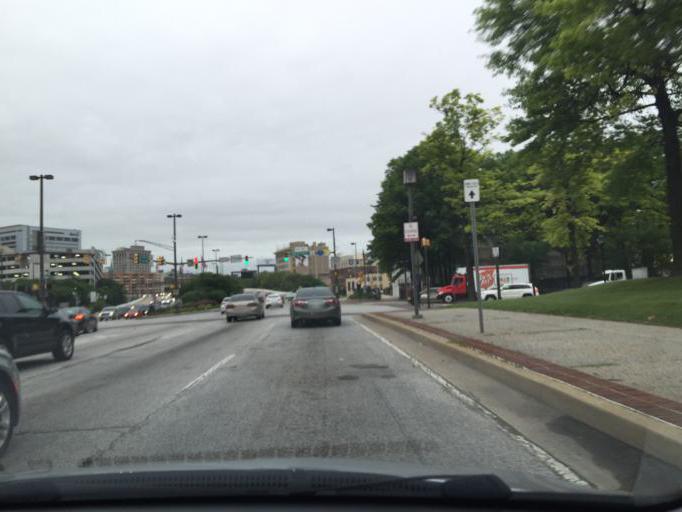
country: US
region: Maryland
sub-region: City of Baltimore
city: Baltimore
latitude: 39.2903
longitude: -76.6060
